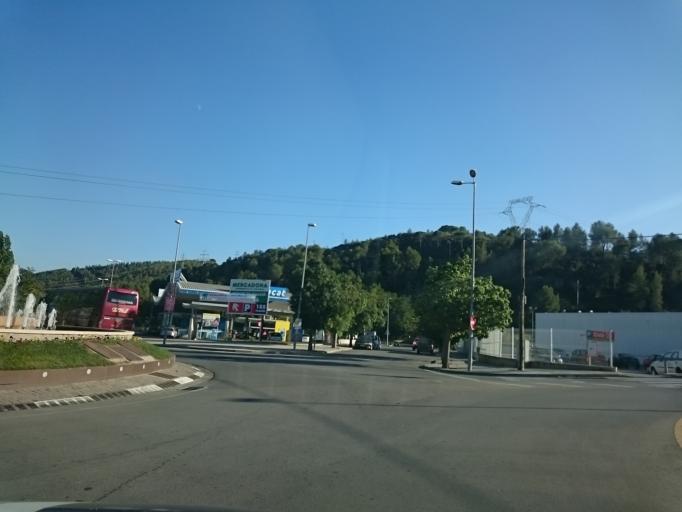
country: ES
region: Catalonia
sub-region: Provincia de Barcelona
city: Sant Andreu de la Barca
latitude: 41.4438
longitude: 1.9811
